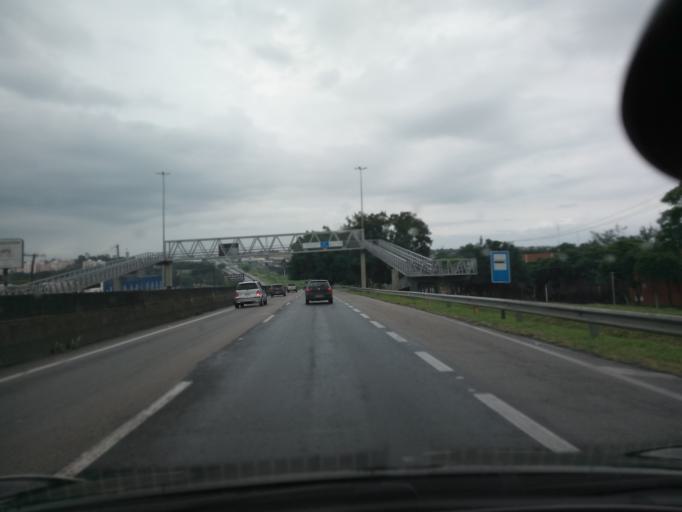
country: BR
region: Sao Paulo
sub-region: Campinas
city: Campinas
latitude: -22.9626
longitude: -47.0981
